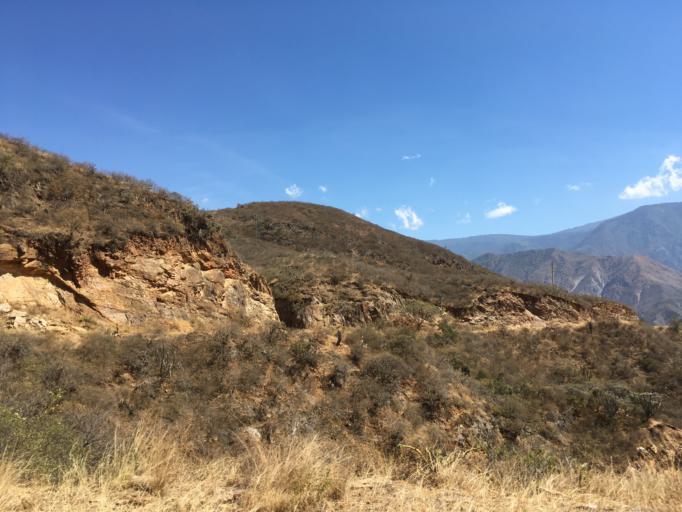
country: CO
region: Santander
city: Aratoca
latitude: 6.7928
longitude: -72.9977
